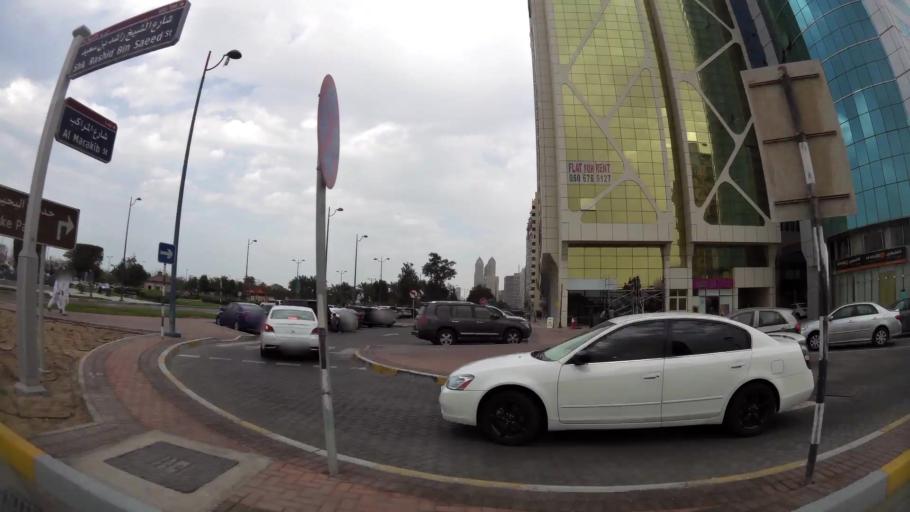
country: AE
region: Abu Dhabi
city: Abu Dhabi
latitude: 24.4902
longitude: 54.3539
